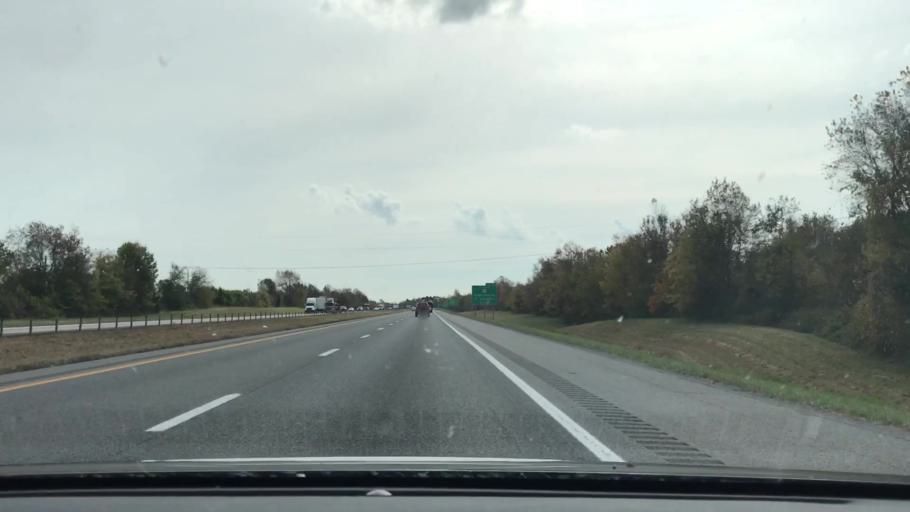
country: US
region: Kentucky
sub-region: Christian County
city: Oak Grove
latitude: 36.7247
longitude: -87.4867
